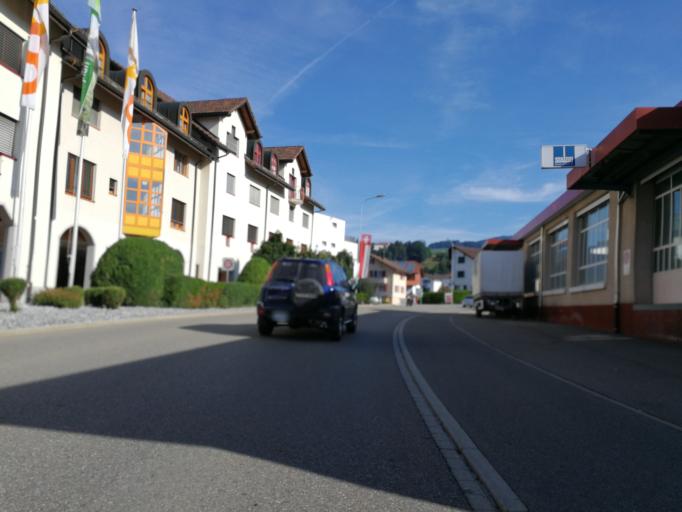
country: CH
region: Saint Gallen
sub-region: Wahlkreis See-Gaster
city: Gommiswald
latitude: 47.2332
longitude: 9.0207
